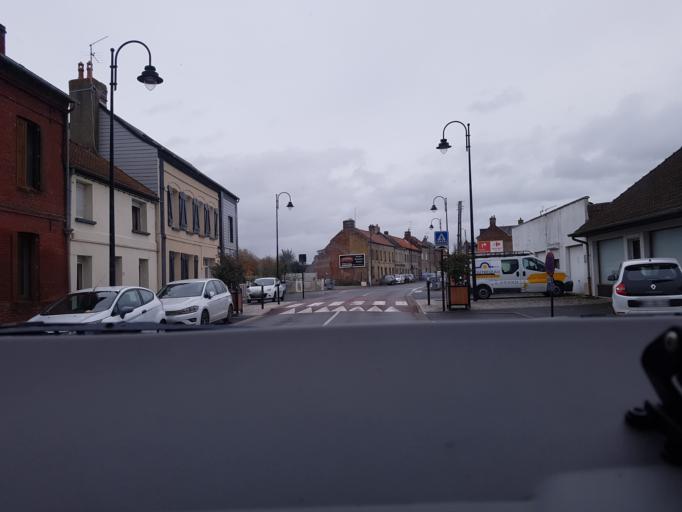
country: FR
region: Picardie
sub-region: Departement de la Somme
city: Abbeville
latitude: 50.1100
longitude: 1.8081
